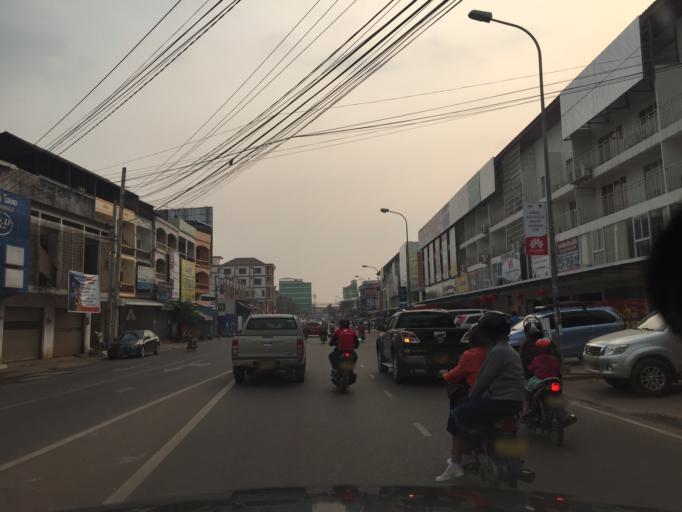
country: LA
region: Vientiane
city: Vientiane
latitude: 17.9751
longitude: 102.6071
